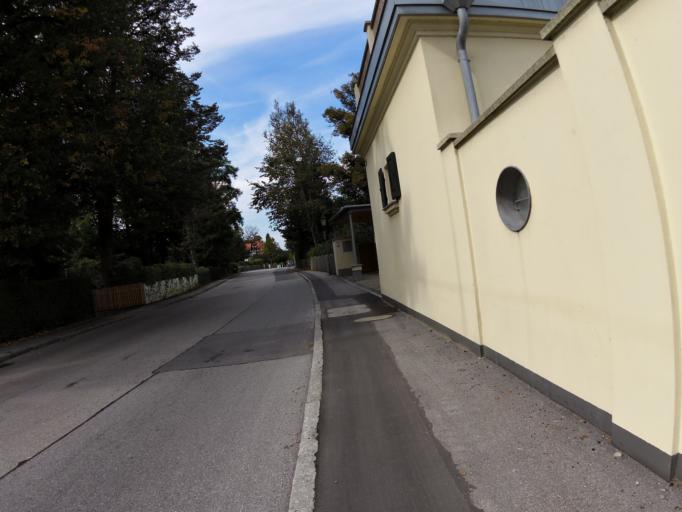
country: DE
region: Bavaria
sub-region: Upper Bavaria
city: Seeshaupt
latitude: 47.8225
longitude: 11.3098
